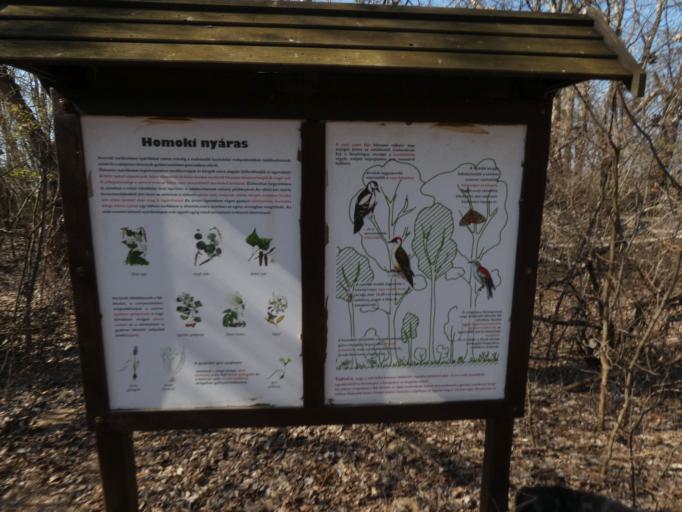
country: HU
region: Pest
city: Farmos
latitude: 47.3627
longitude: 19.8046
